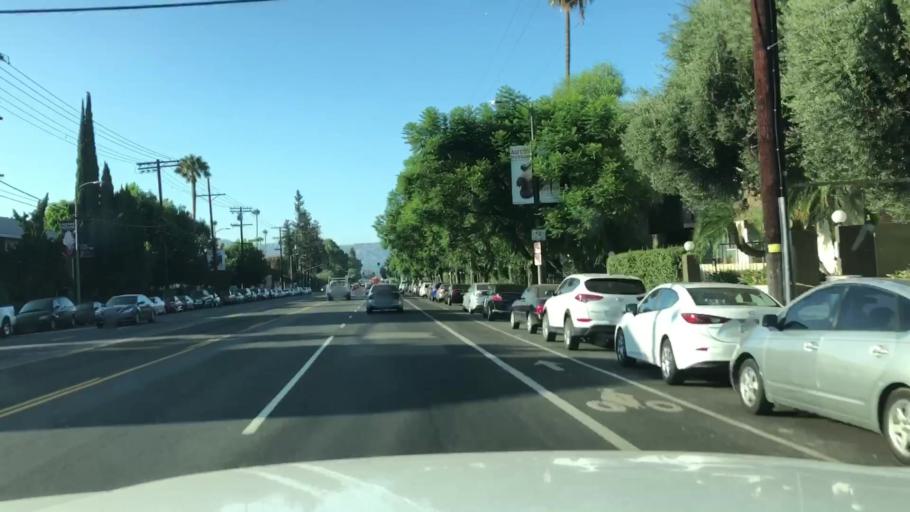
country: US
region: California
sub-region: Los Angeles County
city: Northridge
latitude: 34.1819
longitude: -118.5359
